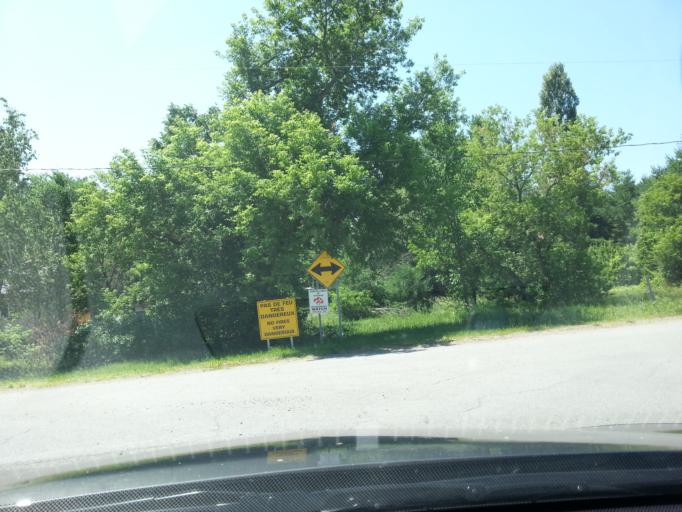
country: CA
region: Ontario
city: Arnprior
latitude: 45.5181
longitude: -76.4064
